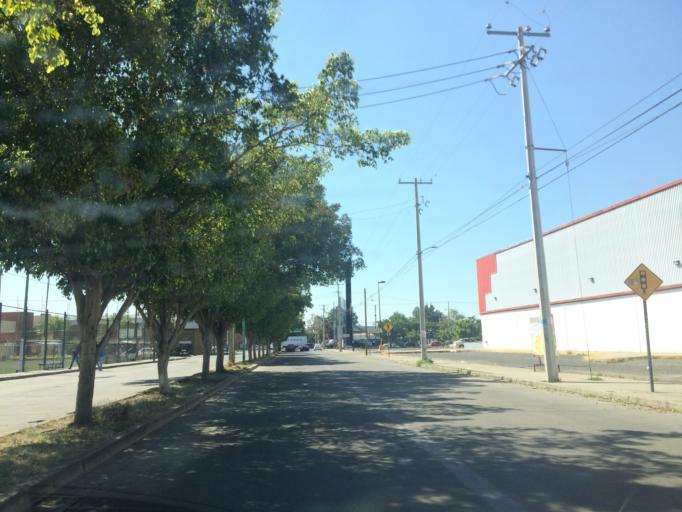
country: MX
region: Guanajuato
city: Leon
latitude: 21.1012
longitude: -101.6704
